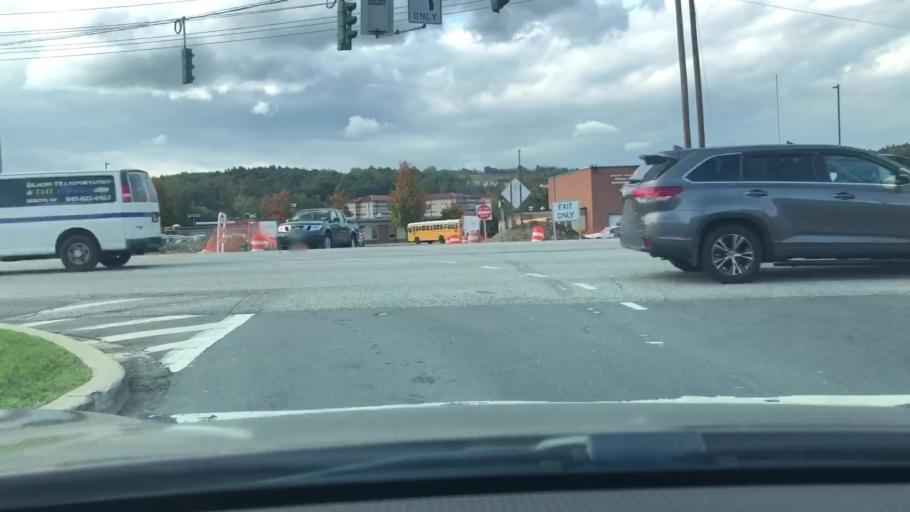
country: US
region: New York
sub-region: Orange County
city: Central Valley
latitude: 41.3181
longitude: -74.1300
